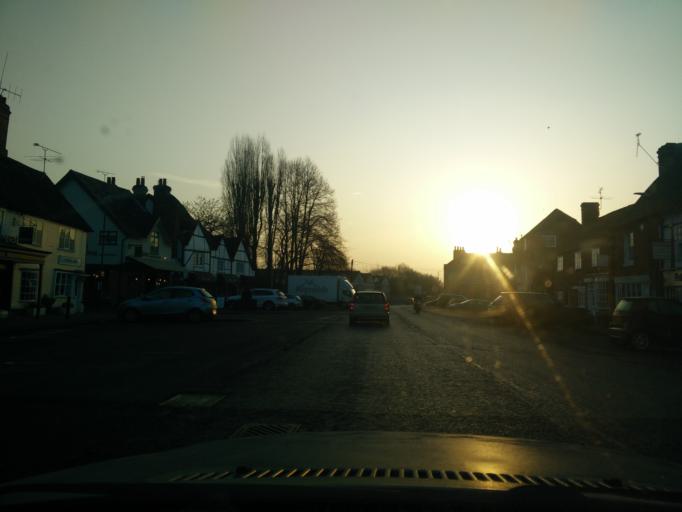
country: GB
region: England
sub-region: Buckinghamshire
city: Amersham
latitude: 51.6662
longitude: -0.6151
